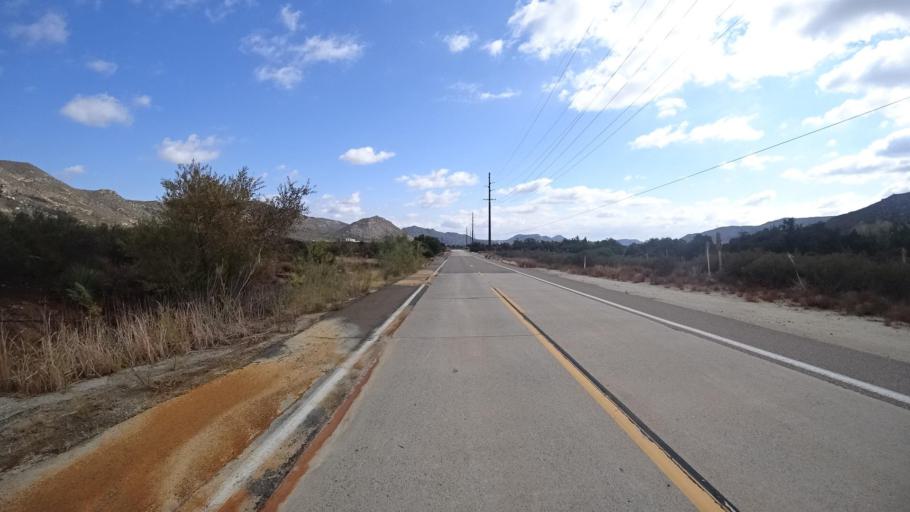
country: US
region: California
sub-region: San Diego County
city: Pine Valley
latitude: 32.7690
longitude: -116.4916
